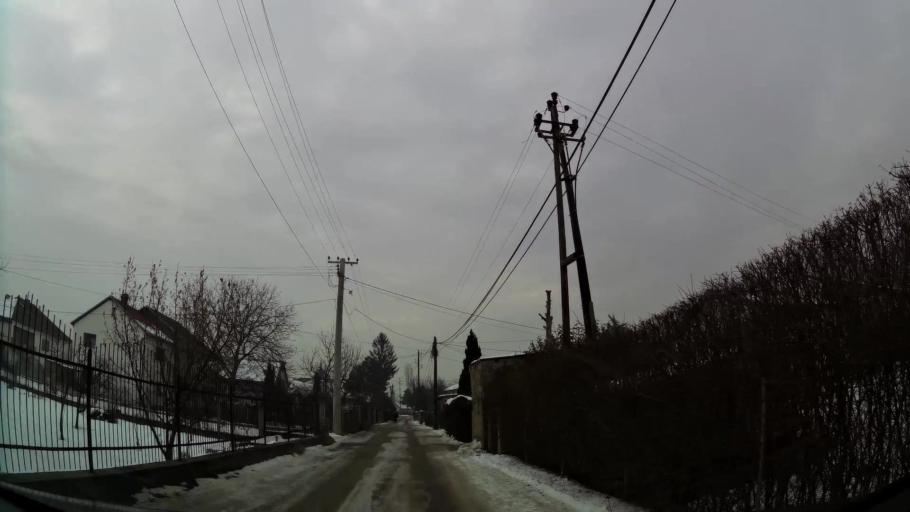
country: MK
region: Saraj
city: Saraj
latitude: 42.0326
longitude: 21.3529
